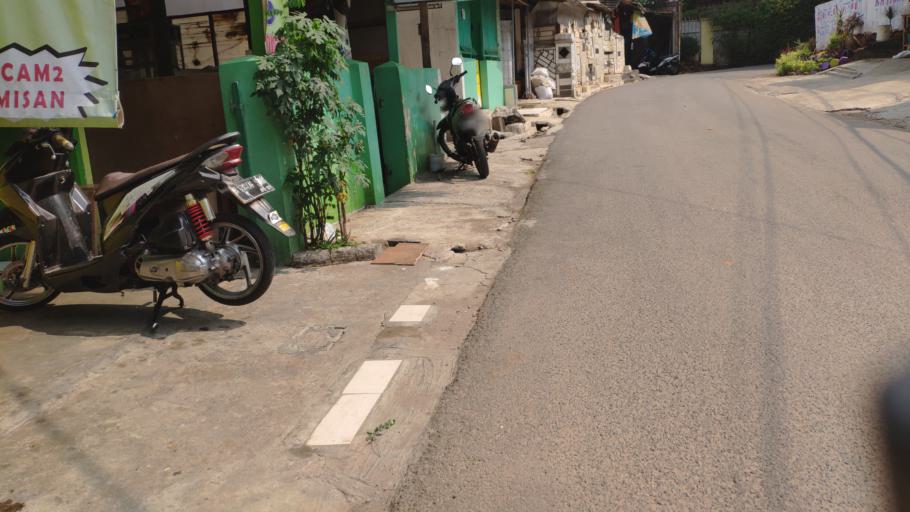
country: ID
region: Jakarta Raya
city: Jakarta
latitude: -6.3065
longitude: 106.8288
